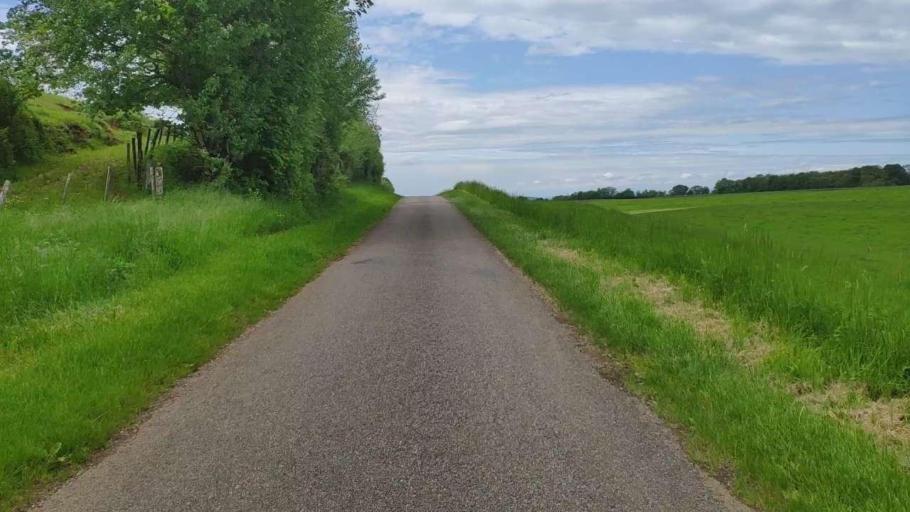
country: FR
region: Franche-Comte
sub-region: Departement du Jura
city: Poligny
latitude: 46.7691
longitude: 5.6489
